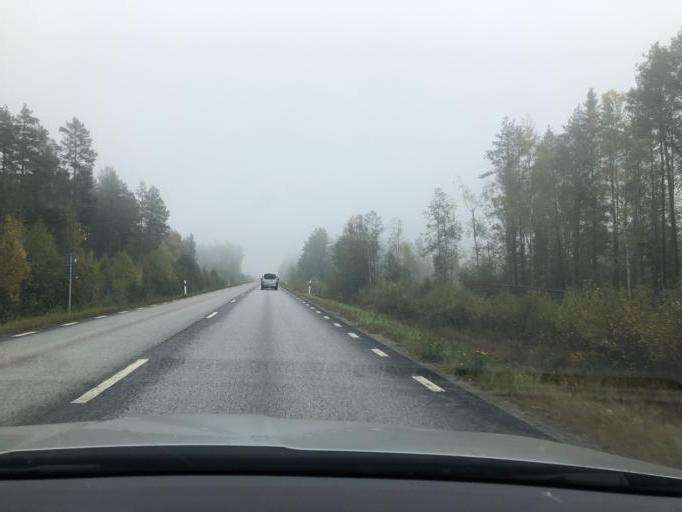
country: SE
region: Uppsala
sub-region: Tierps Kommun
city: Tierp
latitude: 60.3079
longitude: 17.5554
